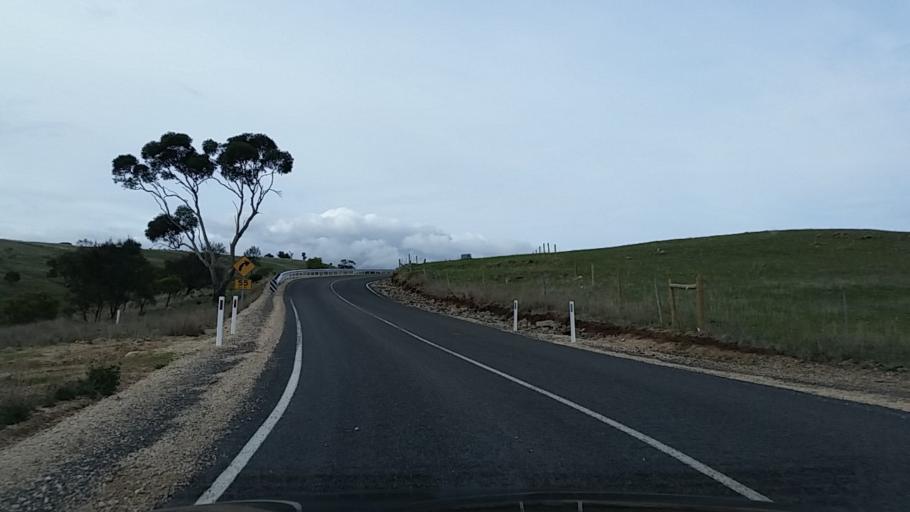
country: AU
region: South Australia
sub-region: Mount Barker
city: Callington
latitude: -35.0153
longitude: 139.0533
